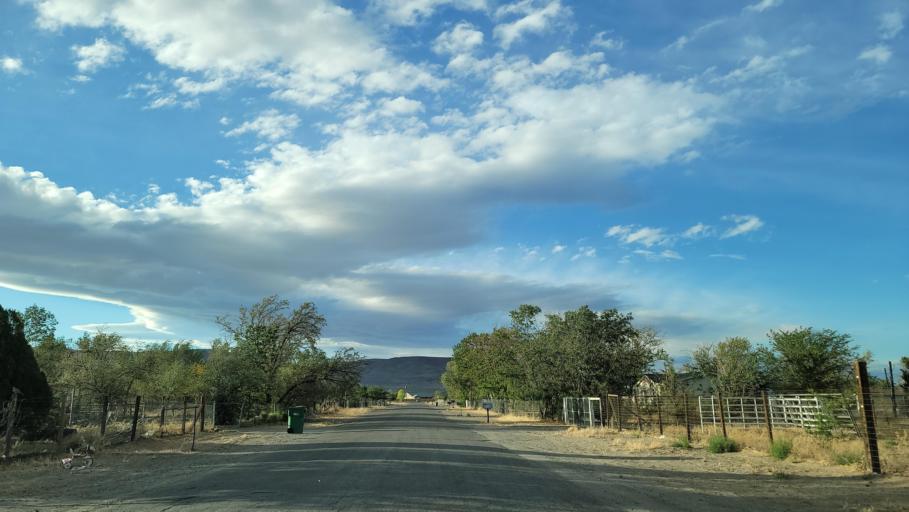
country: US
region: Nevada
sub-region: Lyon County
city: Silver Springs
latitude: 39.3968
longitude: -119.2374
